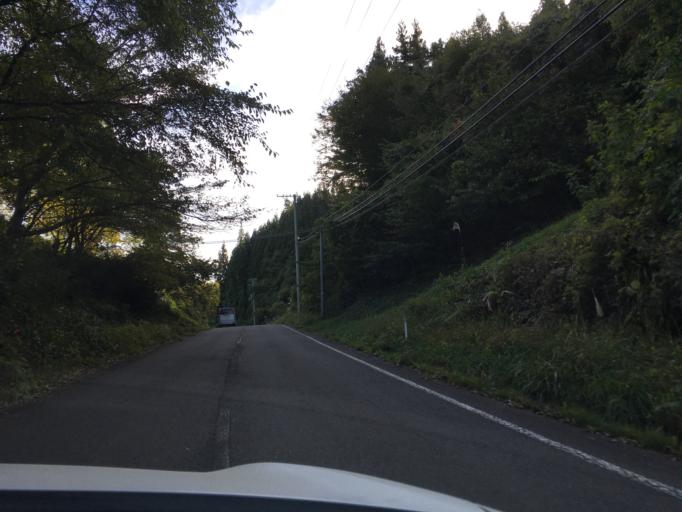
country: JP
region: Fukushima
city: Funehikimachi-funehiki
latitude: 37.2665
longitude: 140.6067
